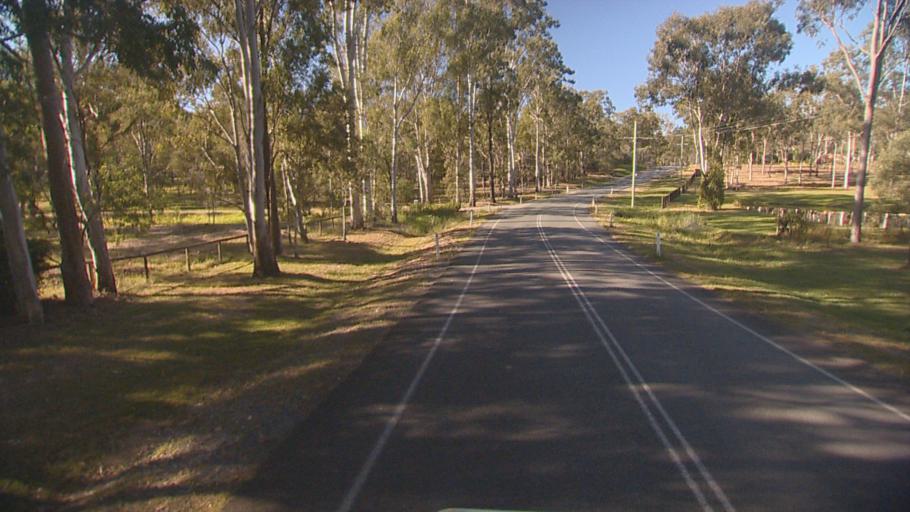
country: AU
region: Queensland
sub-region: Logan
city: Waterford West
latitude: -27.7388
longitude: 153.1484
